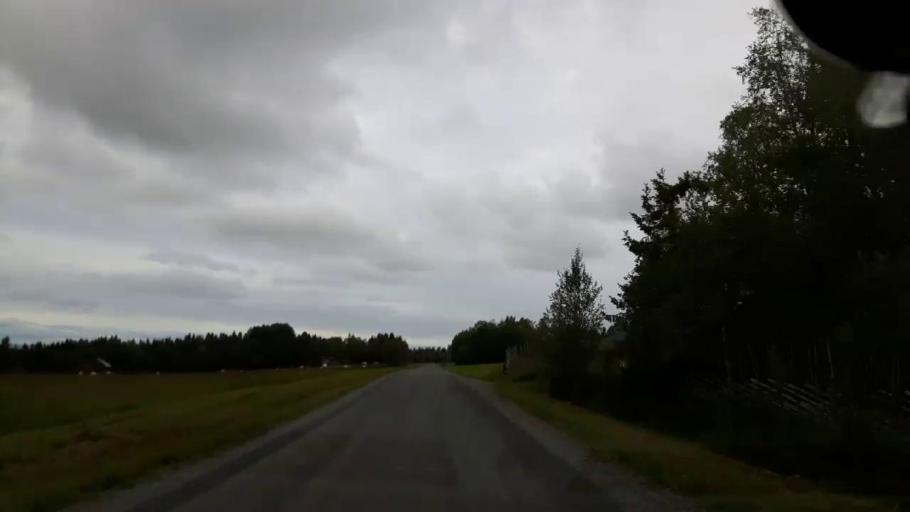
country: SE
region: Jaemtland
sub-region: OEstersunds Kommun
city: Ostersund
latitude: 63.0898
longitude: 14.5546
